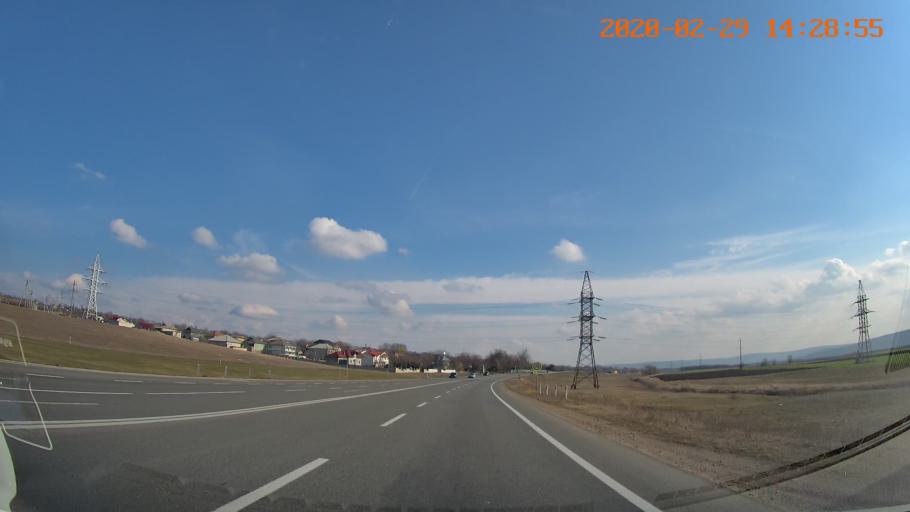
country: MD
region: Orhei
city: Orhei
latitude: 47.4200
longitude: 28.7405
